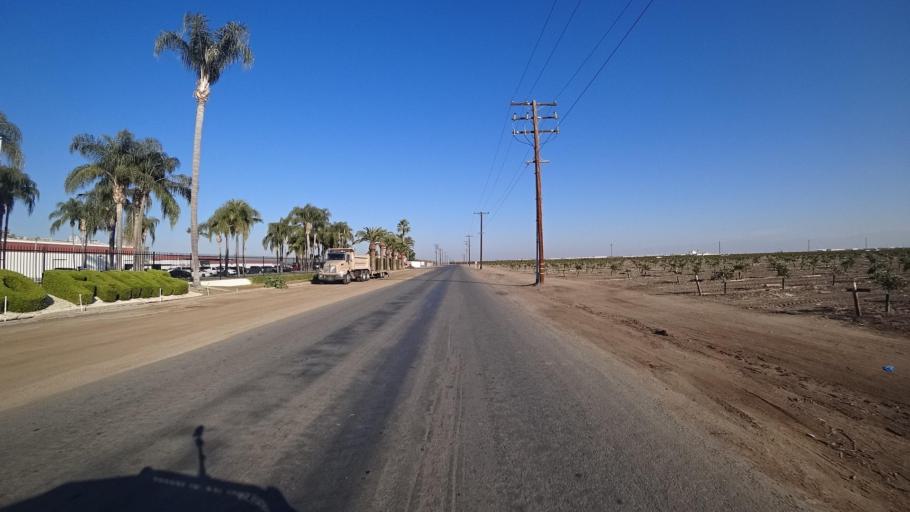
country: US
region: California
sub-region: Tulare County
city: Richgrove
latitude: 35.7883
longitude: -119.1608
